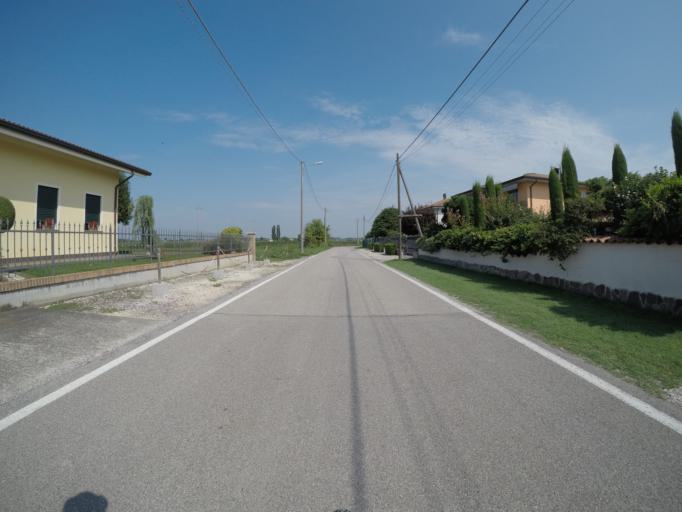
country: IT
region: Veneto
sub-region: Provincia di Rovigo
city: Lendinara
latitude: 45.1028
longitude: 11.5913
